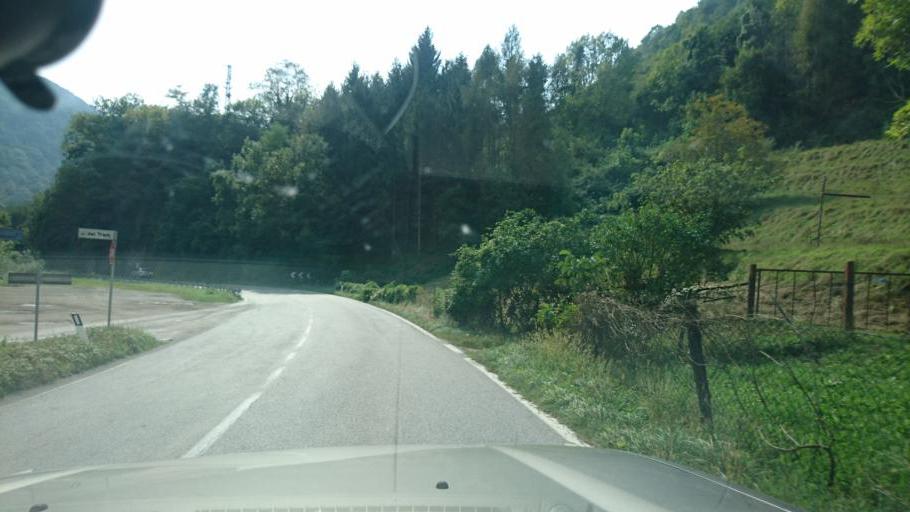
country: IT
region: Lombardy
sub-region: Provincia di Brescia
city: Lavenone
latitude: 45.7289
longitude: 10.4329
